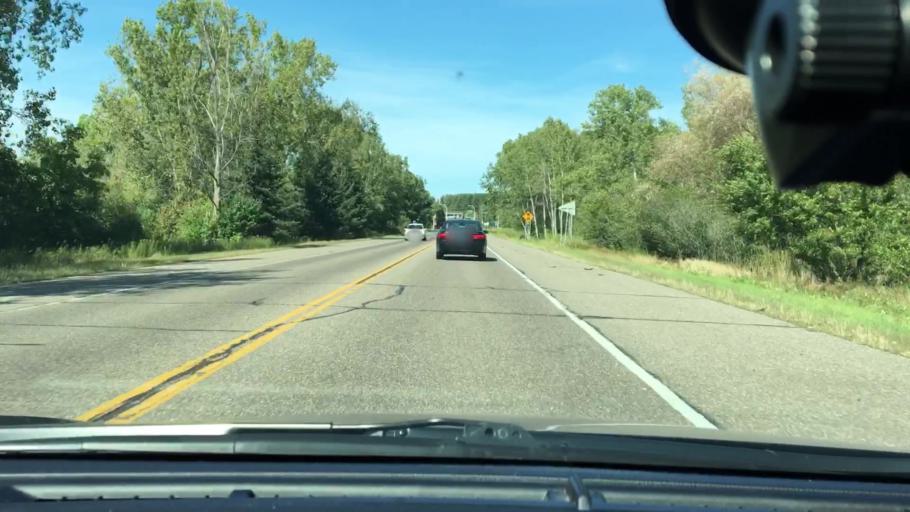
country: US
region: Minnesota
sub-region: Washington County
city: Mahtomedi
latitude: 45.0534
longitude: -92.9475
